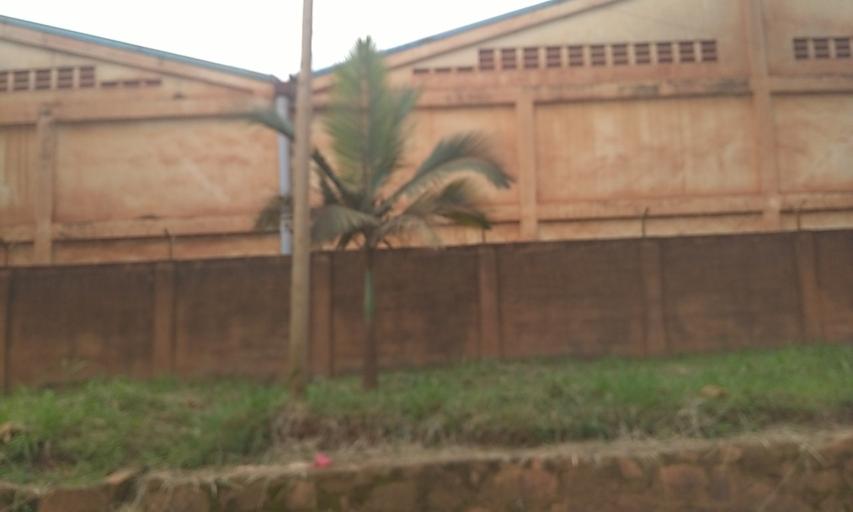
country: UG
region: Central Region
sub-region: Wakiso District
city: Kireka
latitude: 0.3435
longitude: 32.6239
